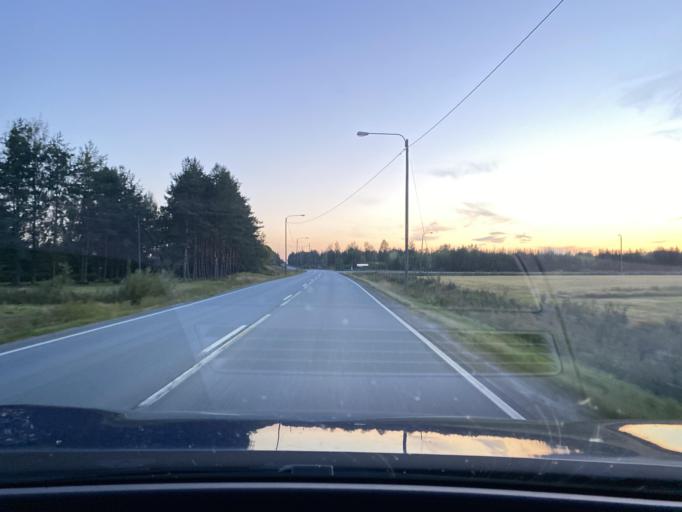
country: FI
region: Southern Ostrobothnia
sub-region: Seinaejoki
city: Kauhava
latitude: 63.1074
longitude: 23.0452
